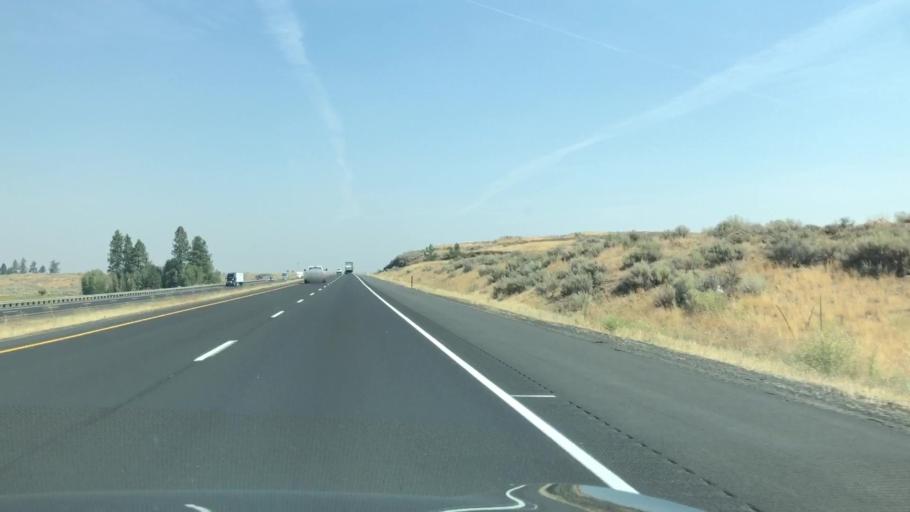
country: US
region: Washington
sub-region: Spokane County
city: Medical Lake
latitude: 47.3777
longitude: -117.8683
